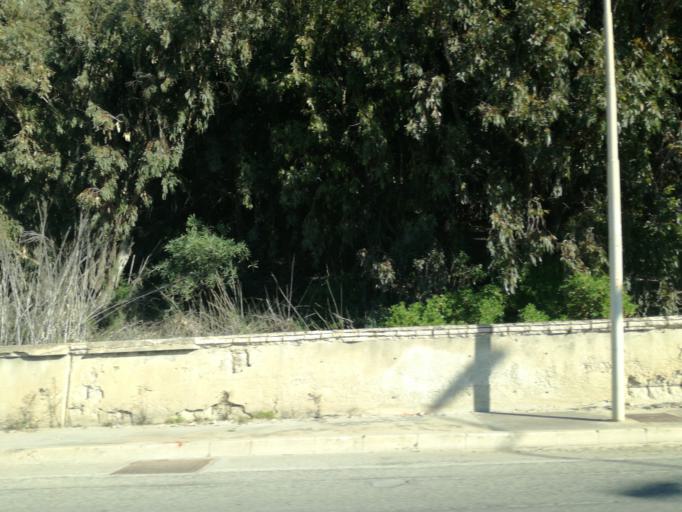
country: IT
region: Sicily
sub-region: Provincia di Caltanissetta
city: Gela
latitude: 37.0688
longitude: 14.2258
